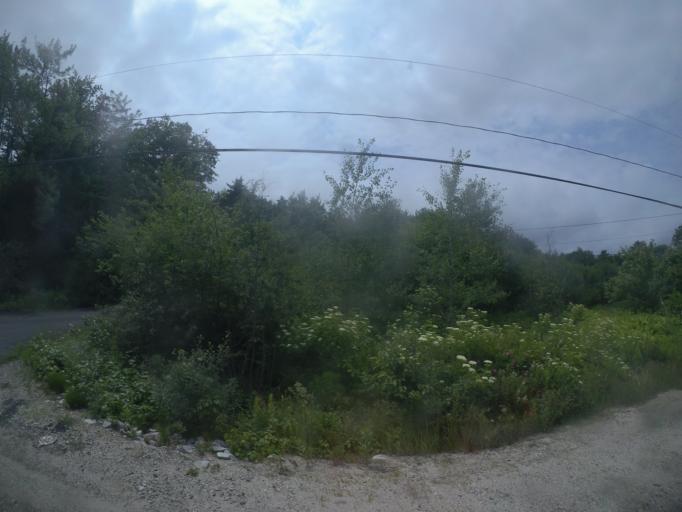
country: US
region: Maine
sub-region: Cumberland County
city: Falmouth
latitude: 43.7484
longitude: -70.2400
